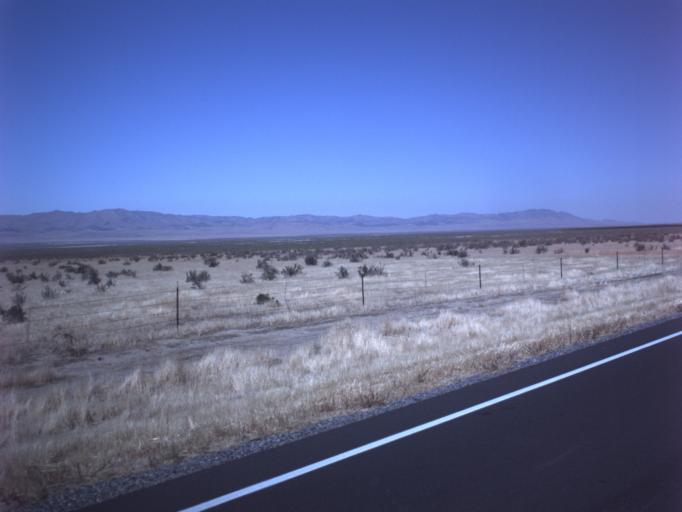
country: US
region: Utah
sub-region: Tooele County
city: Grantsville
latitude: 40.4631
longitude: -112.7471
